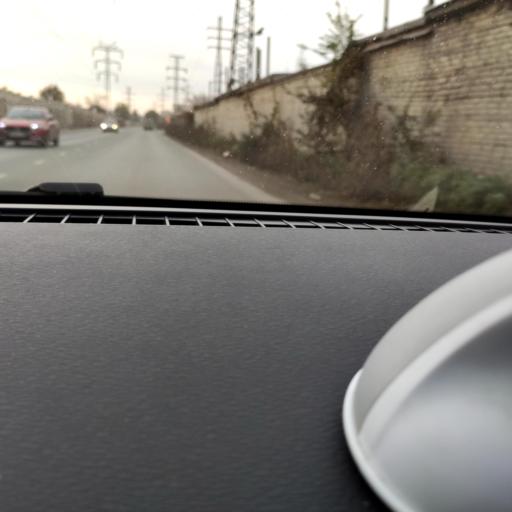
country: RU
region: Samara
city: Petra-Dubrava
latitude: 53.2474
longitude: 50.2930
